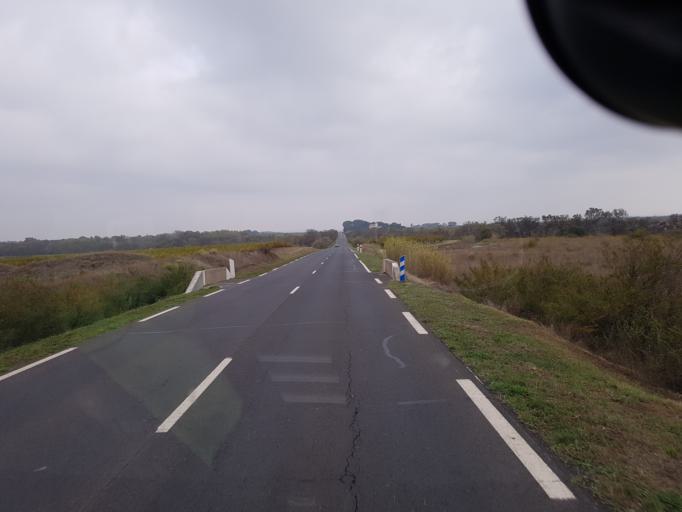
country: FR
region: Languedoc-Roussillon
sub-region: Departement de l'Herault
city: Marseillan
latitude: 43.3802
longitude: 3.5351
